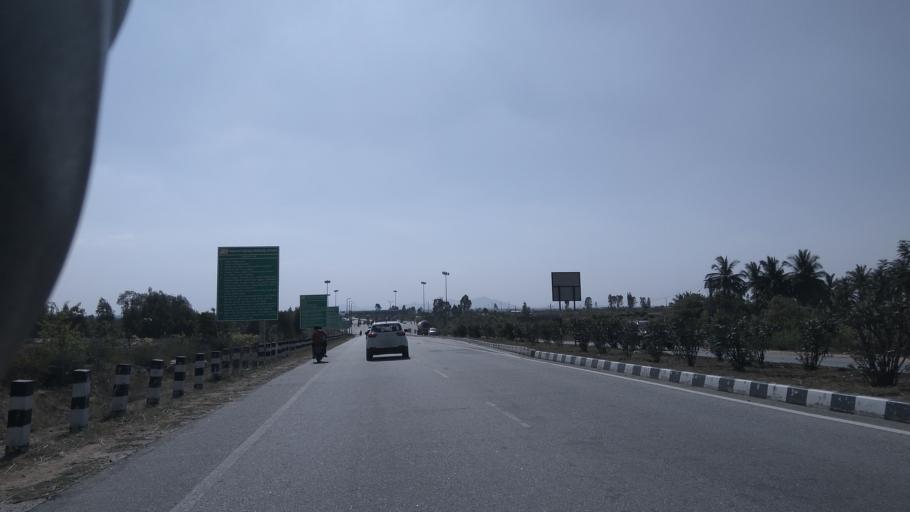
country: IN
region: Karnataka
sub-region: Kolar
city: Mulbagal
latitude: 13.1493
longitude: 78.2953
